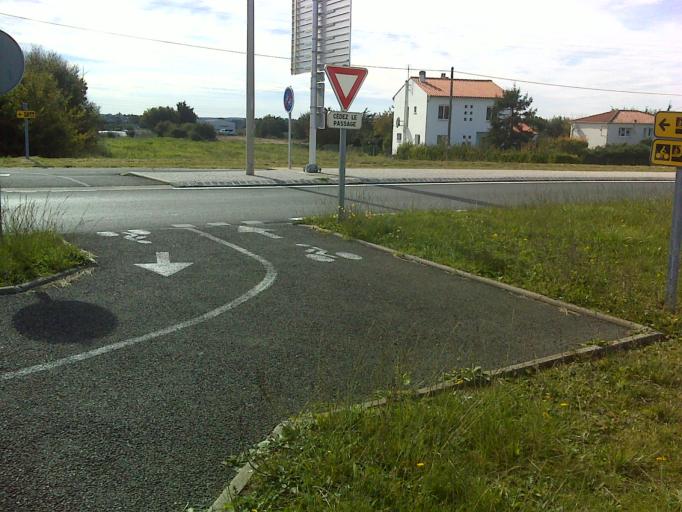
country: FR
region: Poitou-Charentes
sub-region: Departement de la Charente-Maritime
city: Marennes
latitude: 45.8309
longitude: -1.1208
